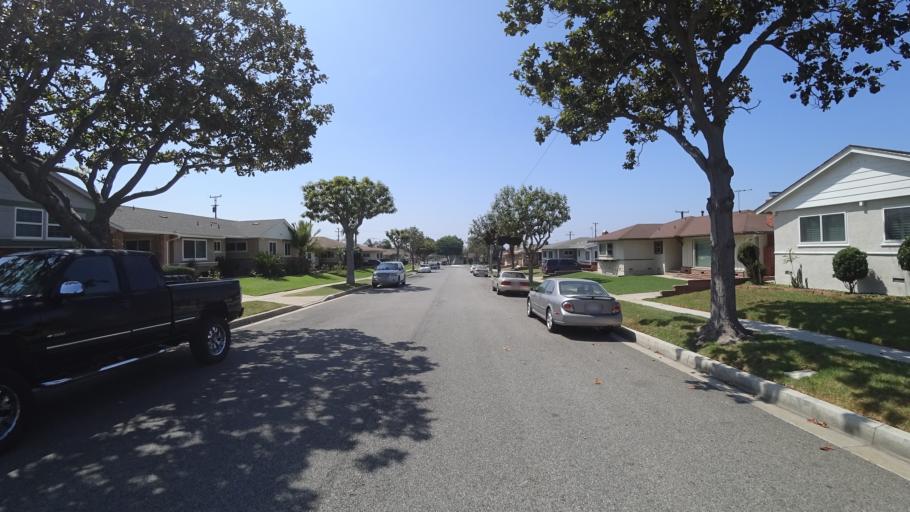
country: US
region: California
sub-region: Los Angeles County
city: Westmont
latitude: 33.9395
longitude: -118.3229
